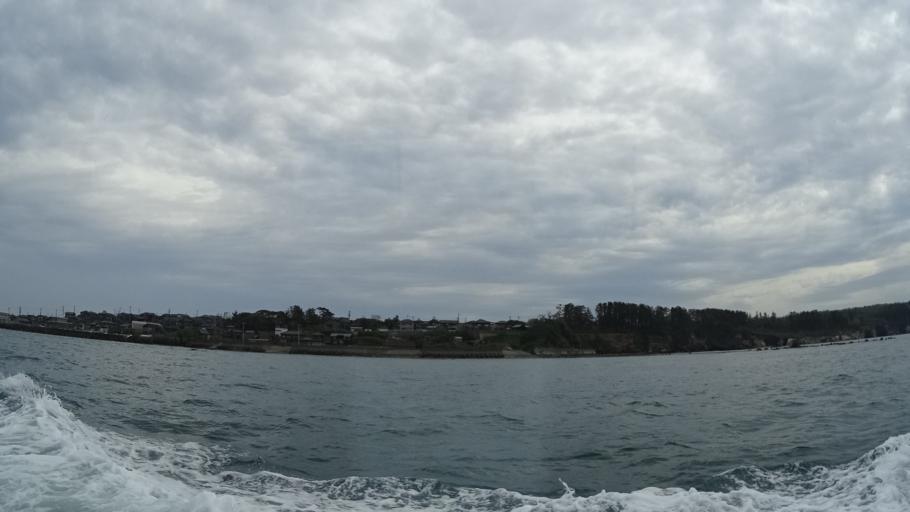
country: JP
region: Fukui
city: Mikuni
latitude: 36.2459
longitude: 136.1217
